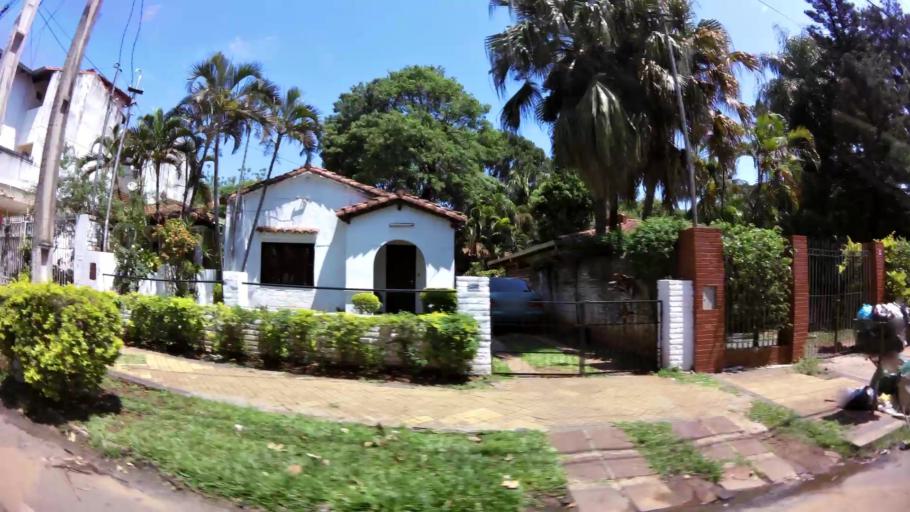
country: PY
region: Central
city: Fernando de la Mora
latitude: -25.3291
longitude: -57.5486
